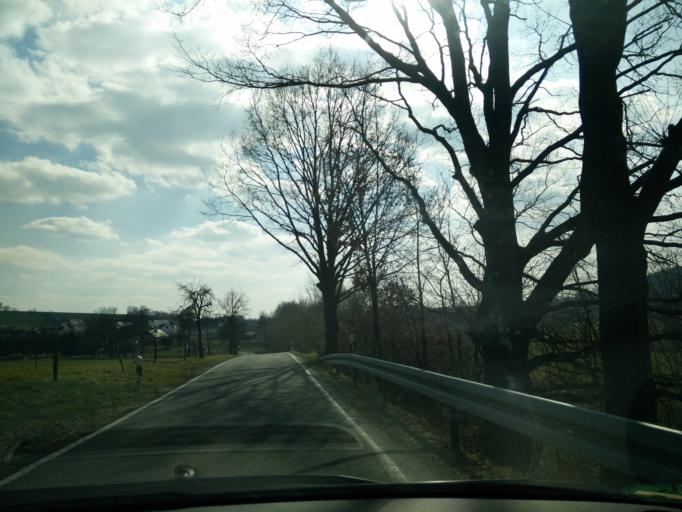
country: DE
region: Saxony
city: Zettlitz
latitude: 51.0879
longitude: 12.8106
